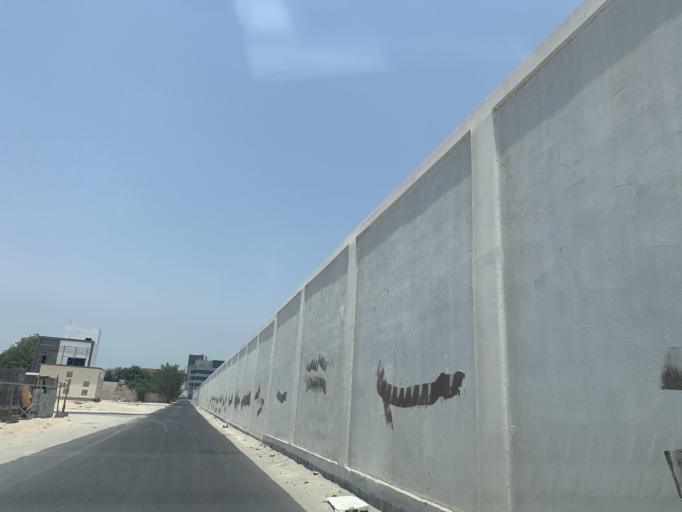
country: BH
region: Manama
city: Jidd Hafs
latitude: 26.2132
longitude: 50.4707
